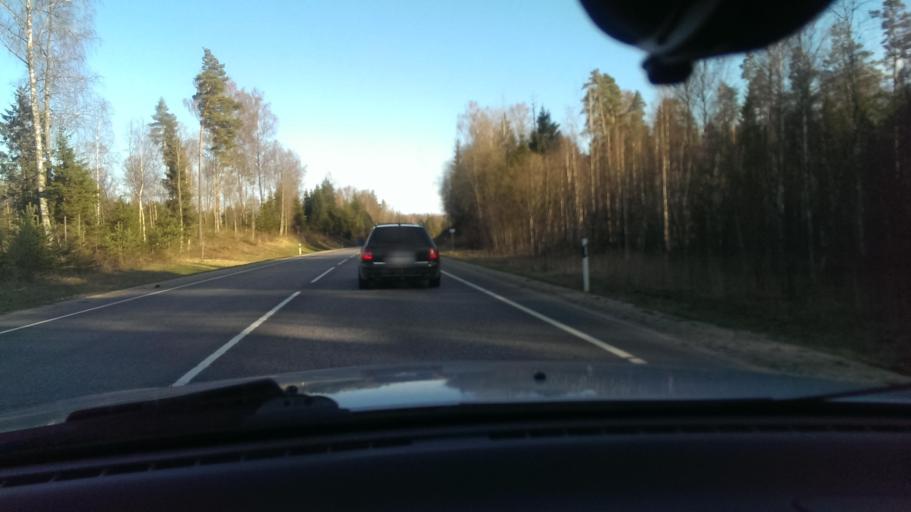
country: EE
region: Tartu
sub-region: UElenurme vald
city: Ulenurme
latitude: 58.1299
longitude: 26.7253
